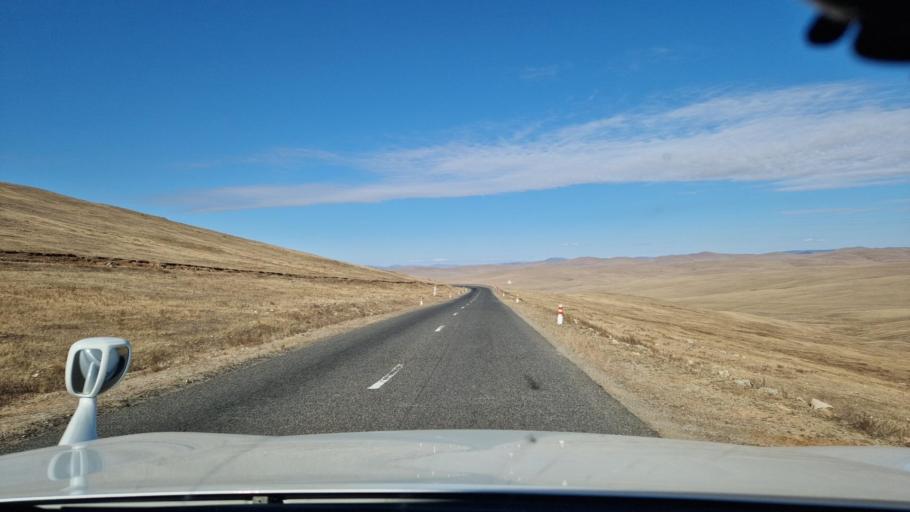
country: MN
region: Hentiy
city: Modot
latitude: 47.5863
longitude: 109.2921
